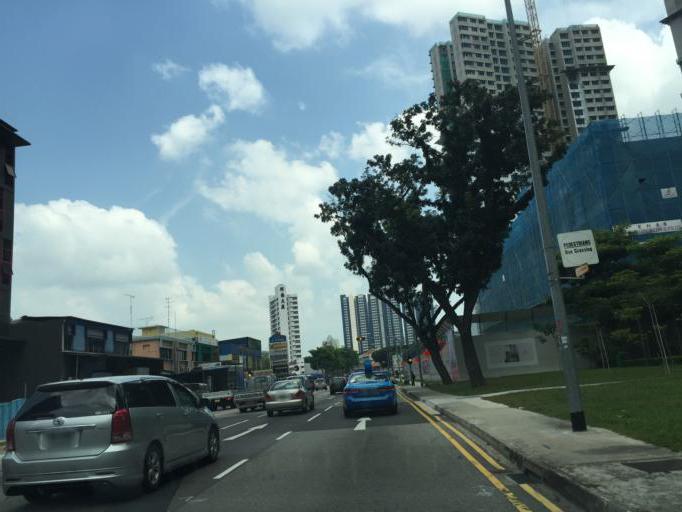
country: SG
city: Singapore
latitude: 1.3159
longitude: 103.8618
